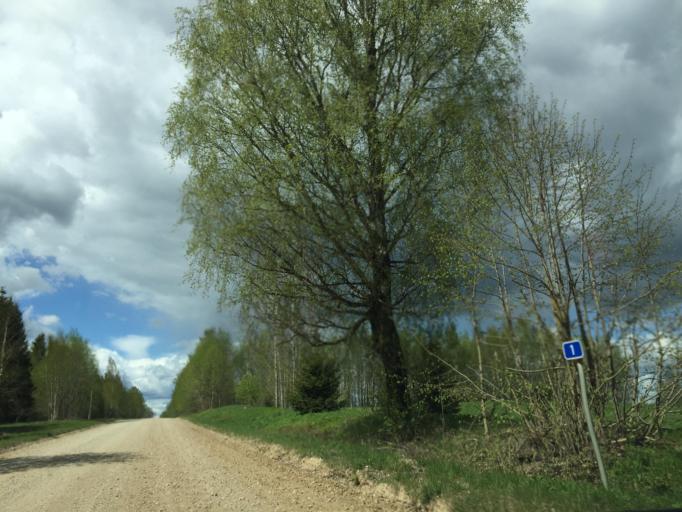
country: LV
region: Madonas Rajons
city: Madona
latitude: 56.9230
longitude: 26.0465
